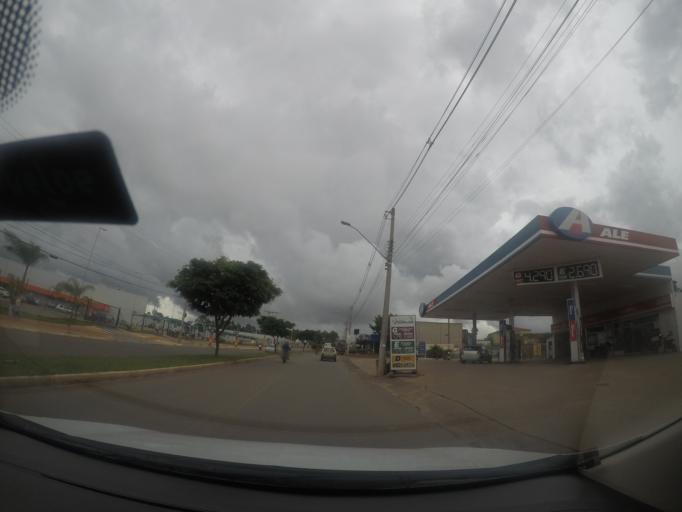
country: BR
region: Goias
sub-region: Trindade
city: Trindade
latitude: -16.6546
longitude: -49.3829
